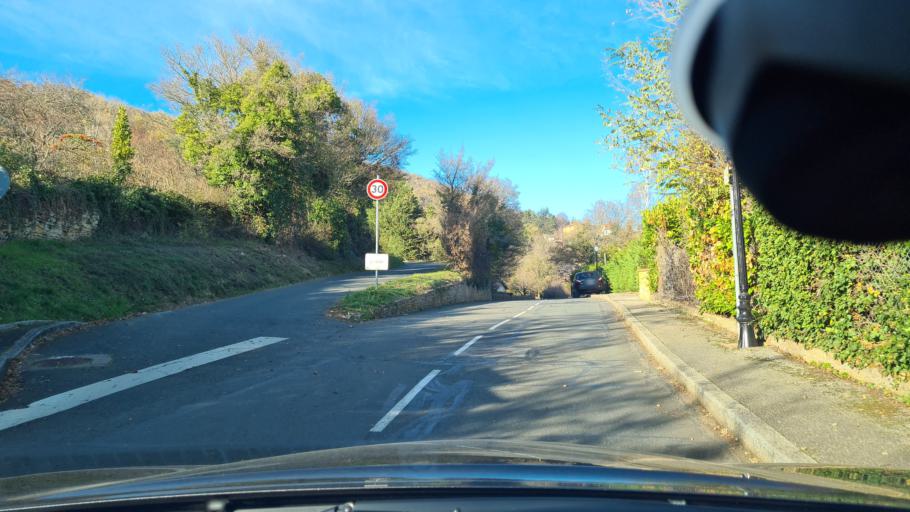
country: FR
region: Rhone-Alpes
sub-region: Departement du Rhone
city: Chasselay
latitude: 45.8563
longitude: 4.7966
